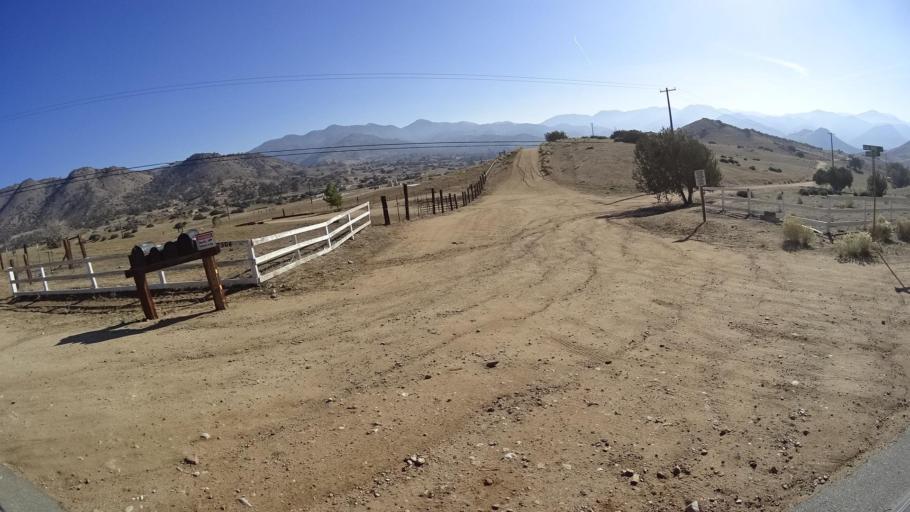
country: US
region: California
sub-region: Kern County
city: Tehachapi
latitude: 35.3482
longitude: -118.3854
